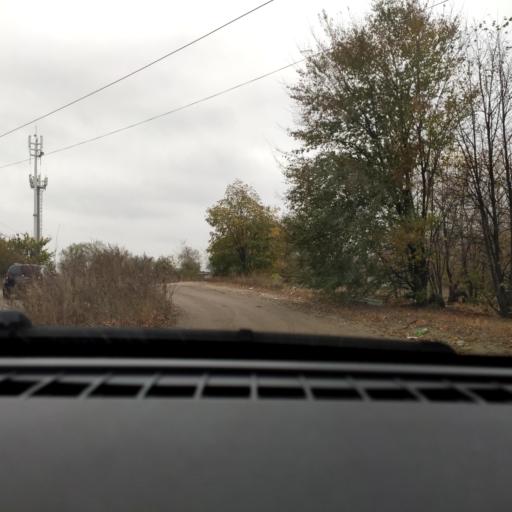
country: RU
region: Voronezj
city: Voronezh
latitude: 51.6634
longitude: 39.2877
